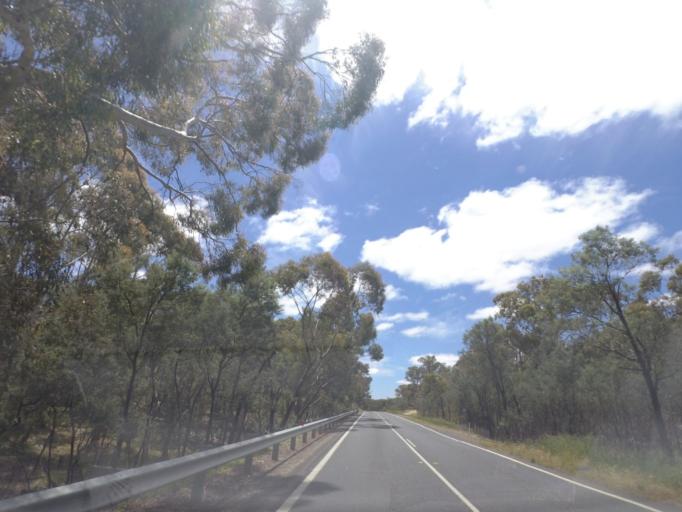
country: AU
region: Victoria
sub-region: Mount Alexander
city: Castlemaine
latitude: -37.2935
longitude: 144.1629
